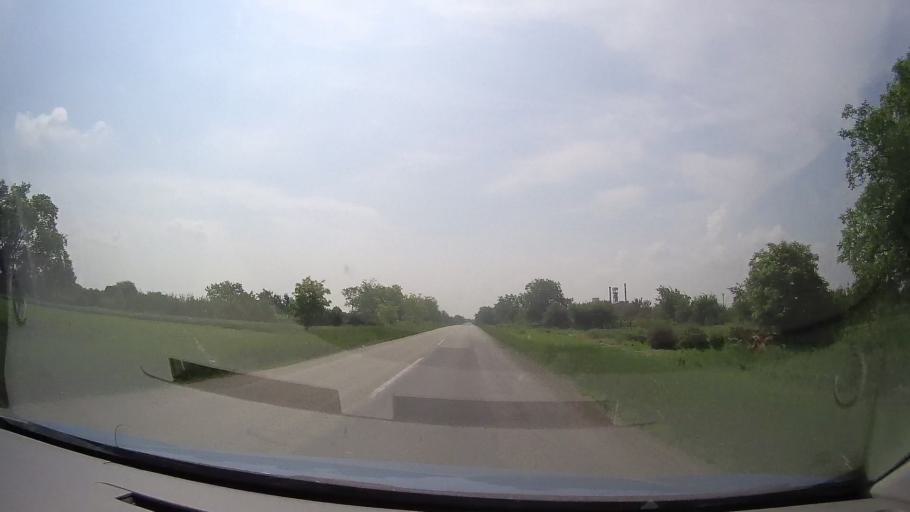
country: RS
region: Autonomna Pokrajina Vojvodina
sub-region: Juznobanatski Okrug
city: Kovacica
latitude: 45.0925
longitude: 20.6321
